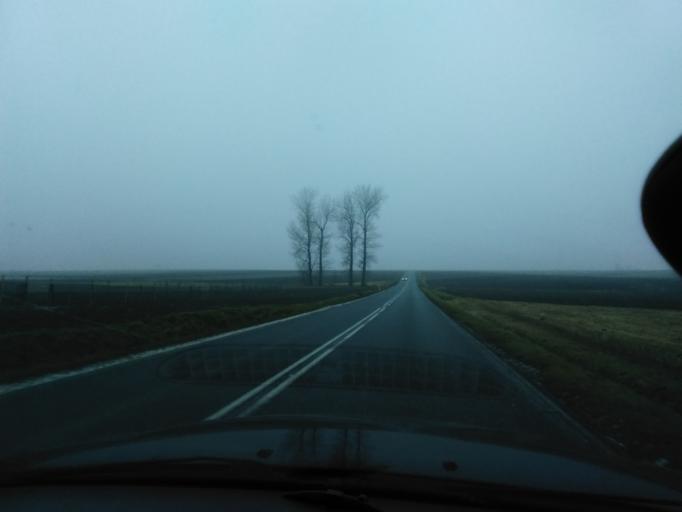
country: PL
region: Subcarpathian Voivodeship
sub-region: Powiat lancucki
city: Markowa
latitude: 50.0350
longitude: 22.3159
